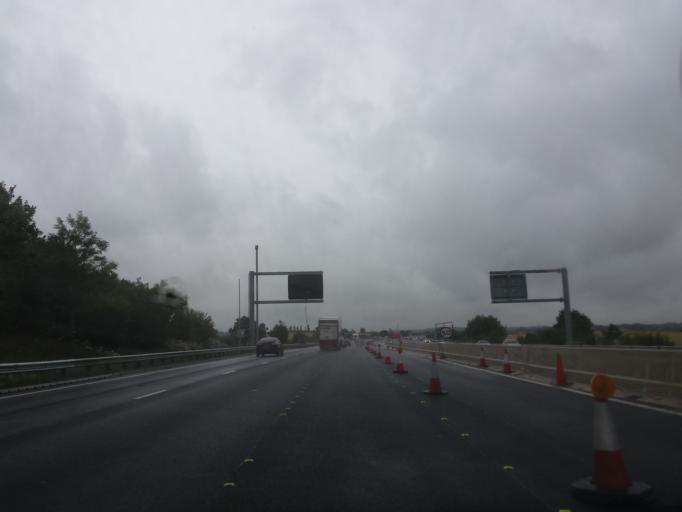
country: GB
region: England
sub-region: Rotherham
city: Wales
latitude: 53.3333
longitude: -1.2854
